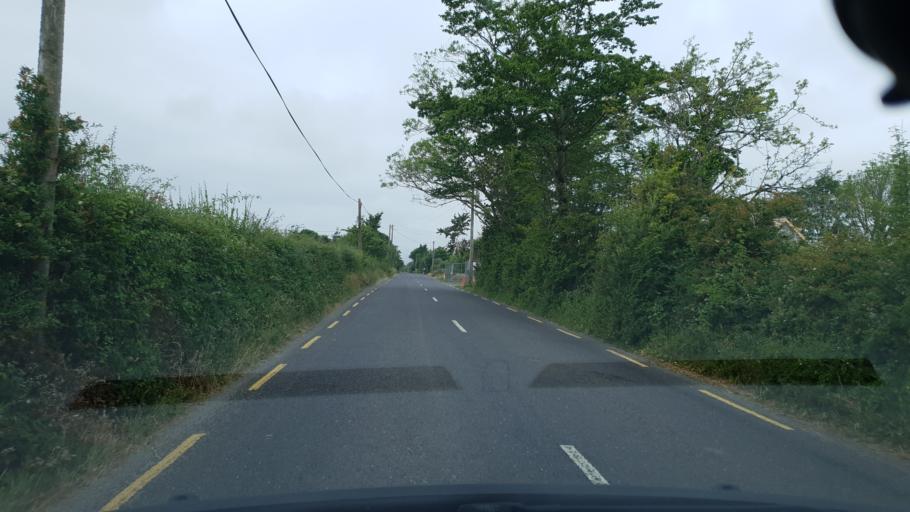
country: IE
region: Munster
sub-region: Ciarrai
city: Tralee
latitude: 52.1637
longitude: -9.6168
